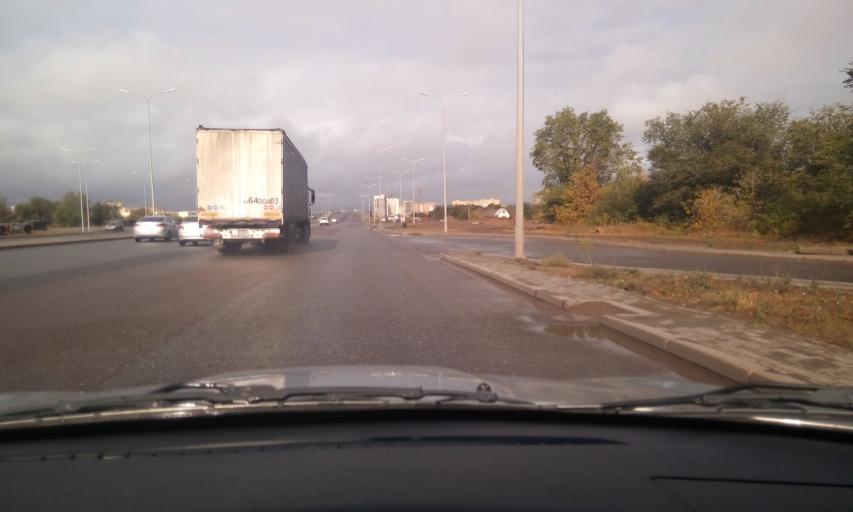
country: KZ
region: Astana Qalasy
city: Astana
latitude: 51.1587
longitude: 71.3729
